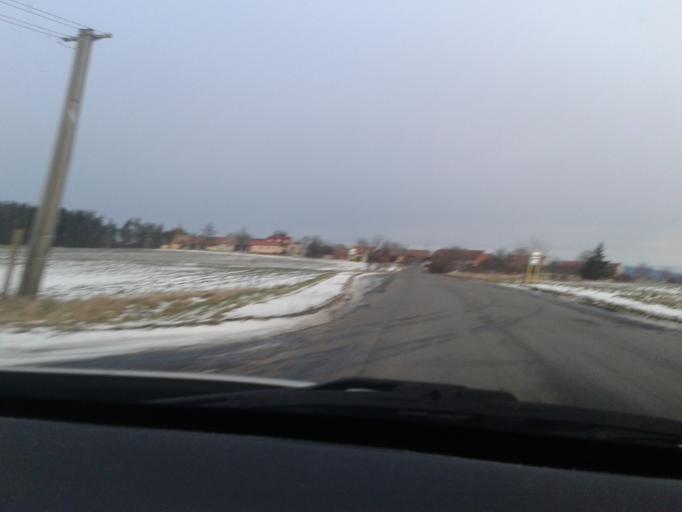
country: CZ
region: Olomoucky
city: Pteni
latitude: 49.5001
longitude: 16.9420
